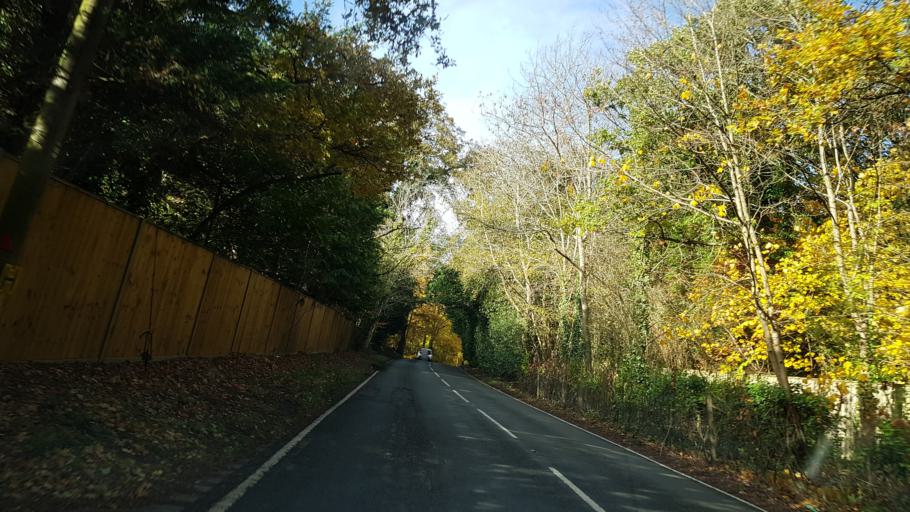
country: GB
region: England
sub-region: Surrey
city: Seale
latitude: 51.1948
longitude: -0.7405
